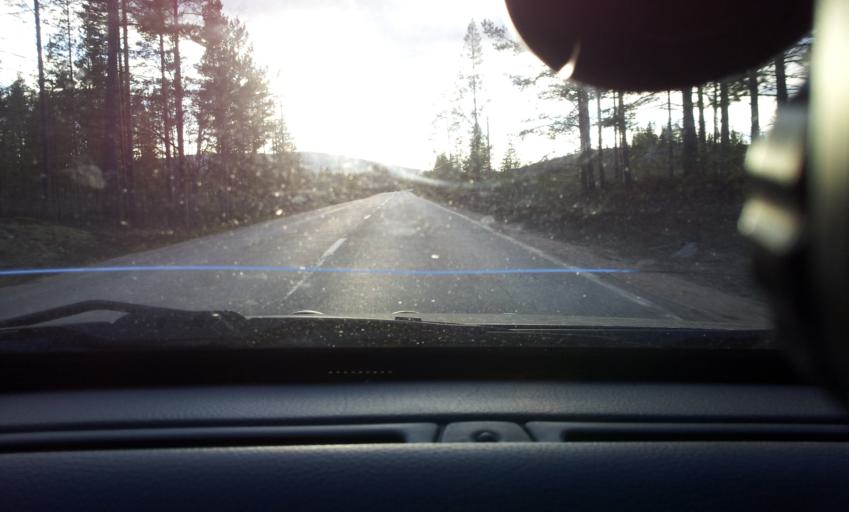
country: SE
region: Jaemtland
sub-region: Harjedalens Kommun
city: Sveg
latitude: 62.1241
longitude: 14.9985
